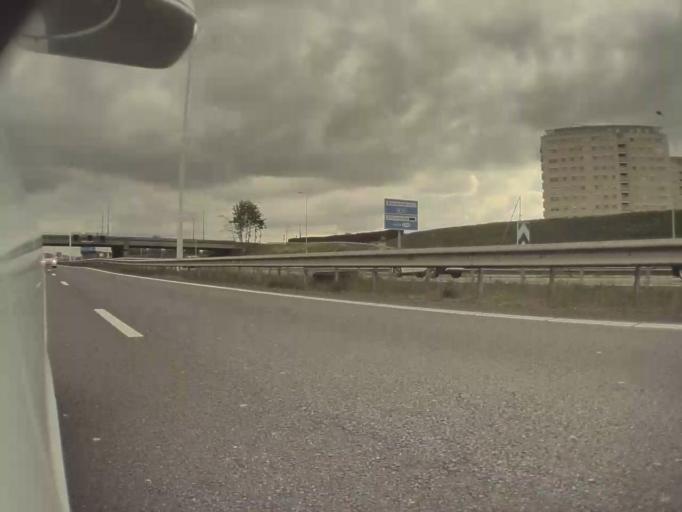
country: NL
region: South Holland
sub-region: Gemeente Capelle aan den IJssel
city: Capelle-West
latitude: 51.8871
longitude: 4.5667
